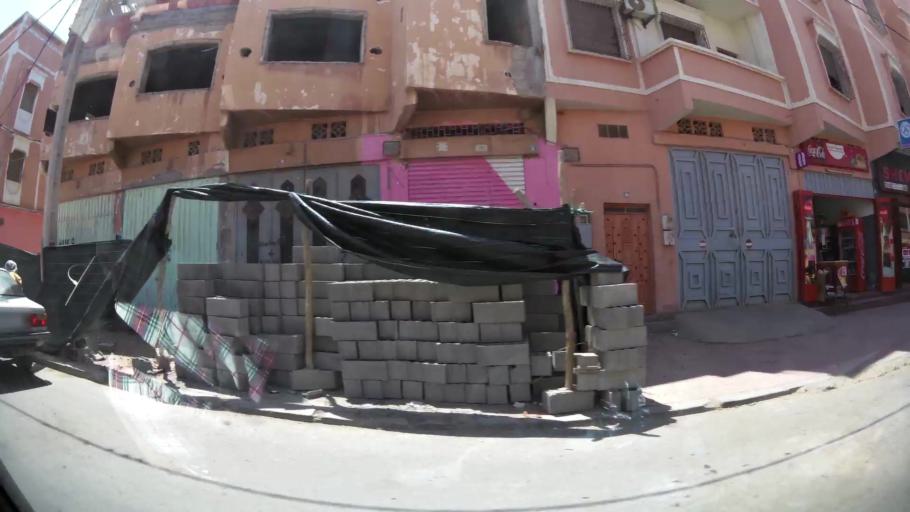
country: MA
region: Souss-Massa-Draa
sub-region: Inezgane-Ait Mellou
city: Inezgane
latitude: 30.3454
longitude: -9.4955
